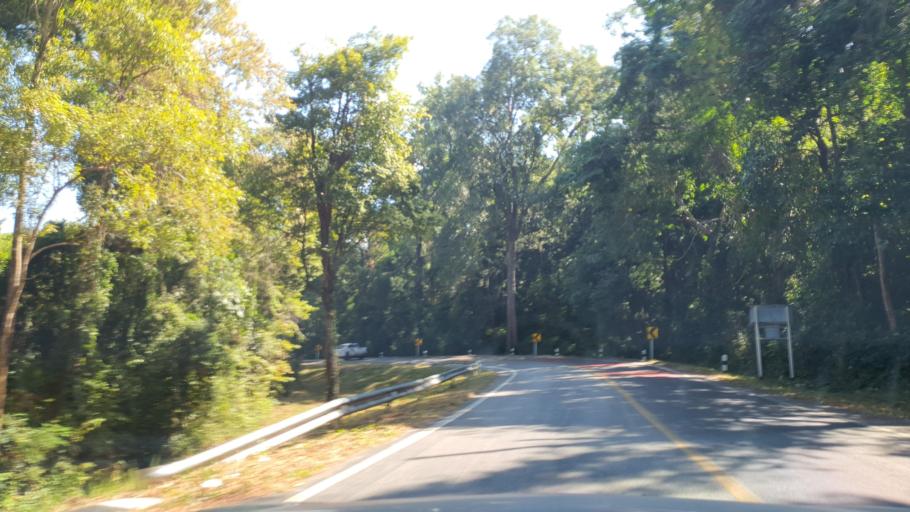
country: TH
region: Kalasin
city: Na Khu
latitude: 16.8433
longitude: 103.9071
